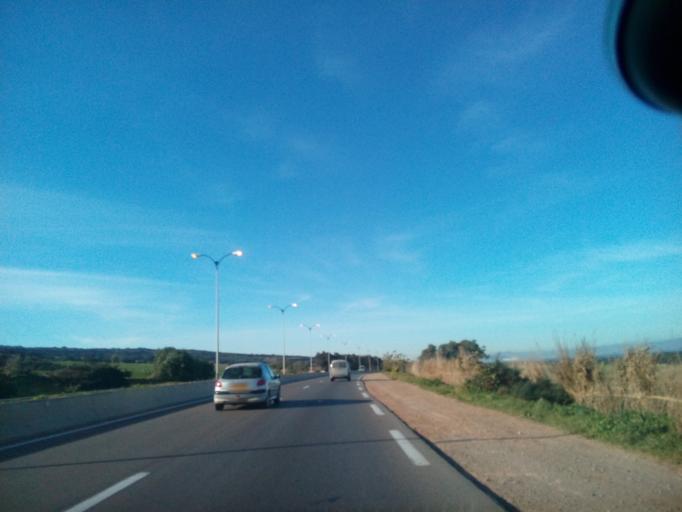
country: DZ
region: Mostaganem
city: Mostaganem
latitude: 35.8055
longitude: -0.0491
